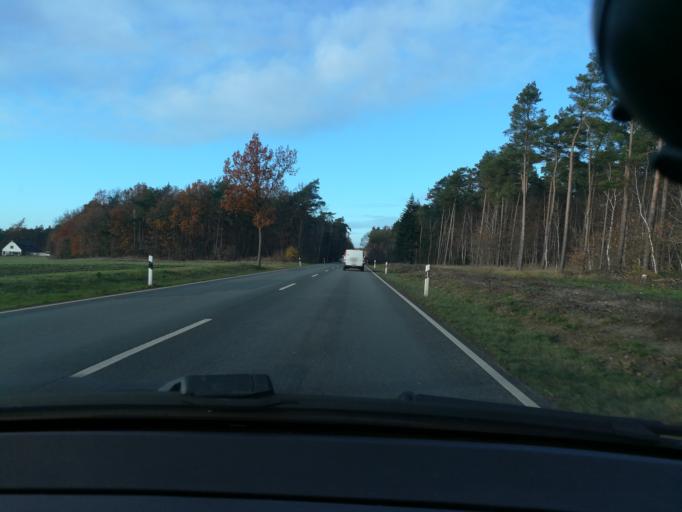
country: DE
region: Lower Saxony
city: Uchte
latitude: 52.5331
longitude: 8.8782
